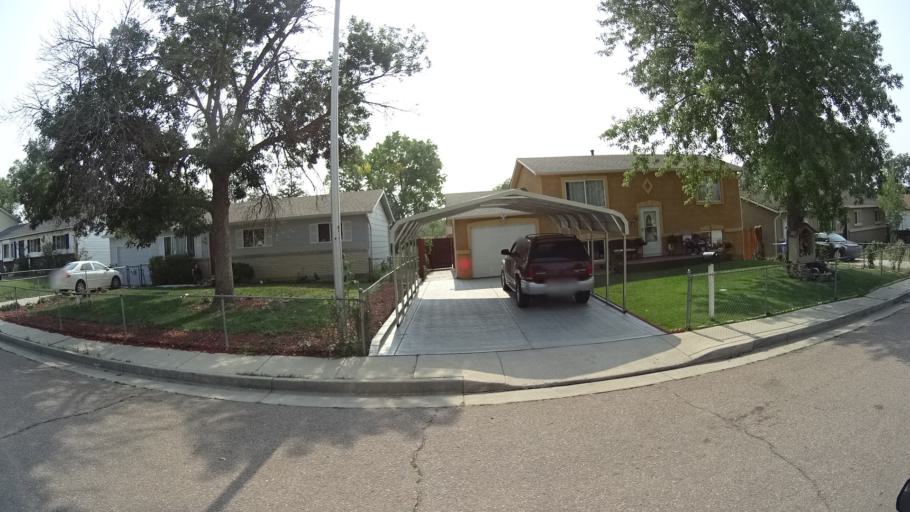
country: US
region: Colorado
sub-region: El Paso County
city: Stratmoor
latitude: 38.8086
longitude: -104.7636
